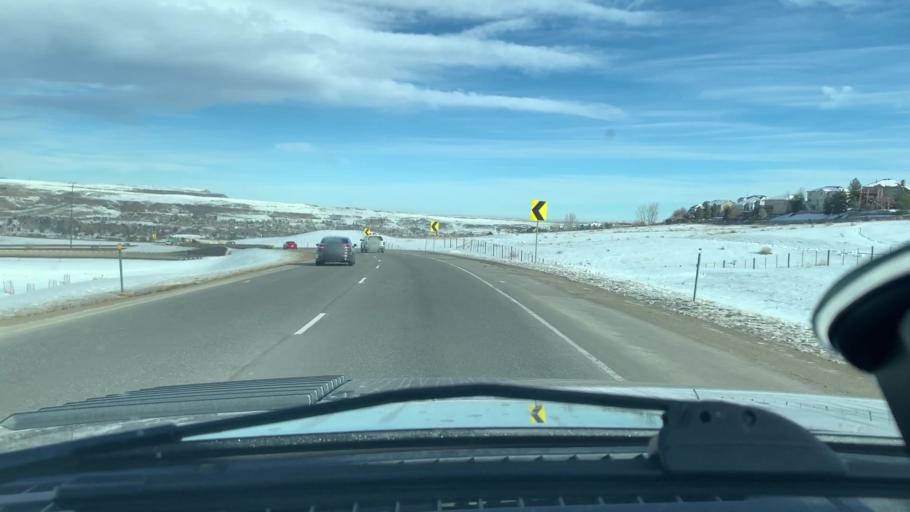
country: US
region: Colorado
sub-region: Jefferson County
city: West Pleasant View
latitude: 39.7108
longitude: -105.1913
